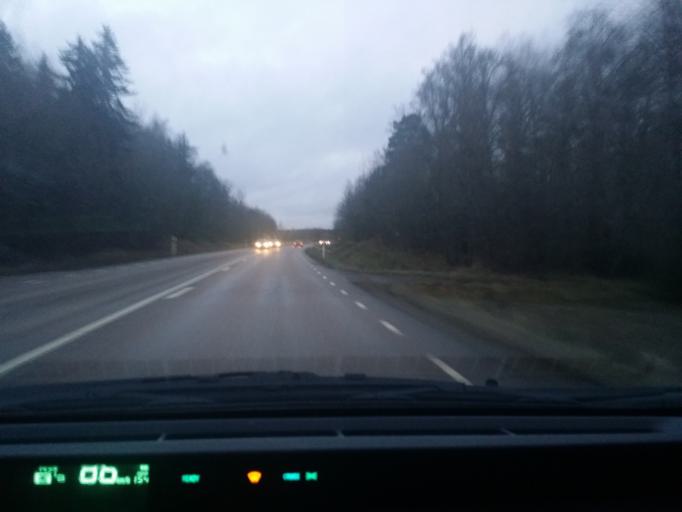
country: SE
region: Soedermanland
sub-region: Eskilstuna Kommun
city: Kvicksund
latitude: 59.4779
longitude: 16.3050
